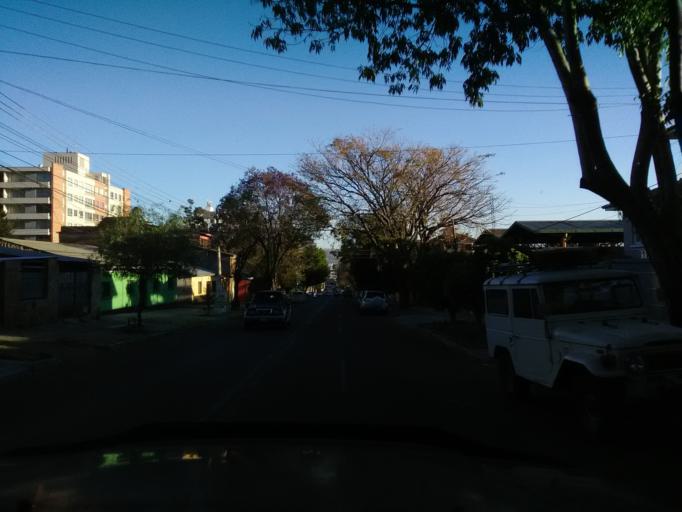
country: BO
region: Cochabamba
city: Cochabamba
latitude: -17.3691
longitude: -66.1511
